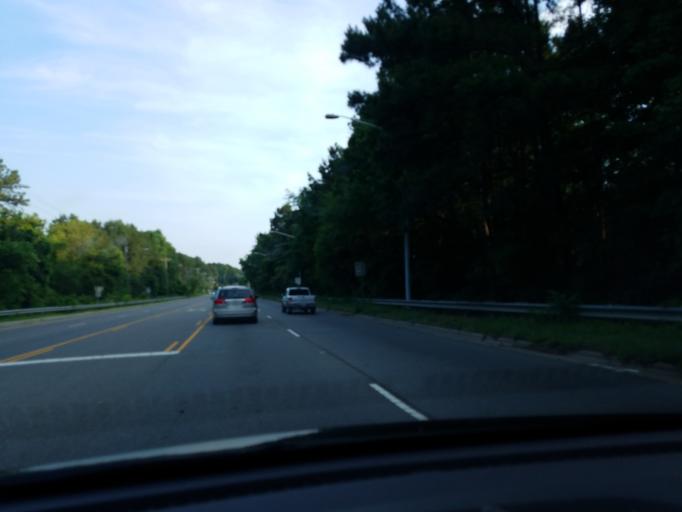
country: US
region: North Carolina
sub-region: Durham County
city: Durham
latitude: 36.0369
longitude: -78.9060
